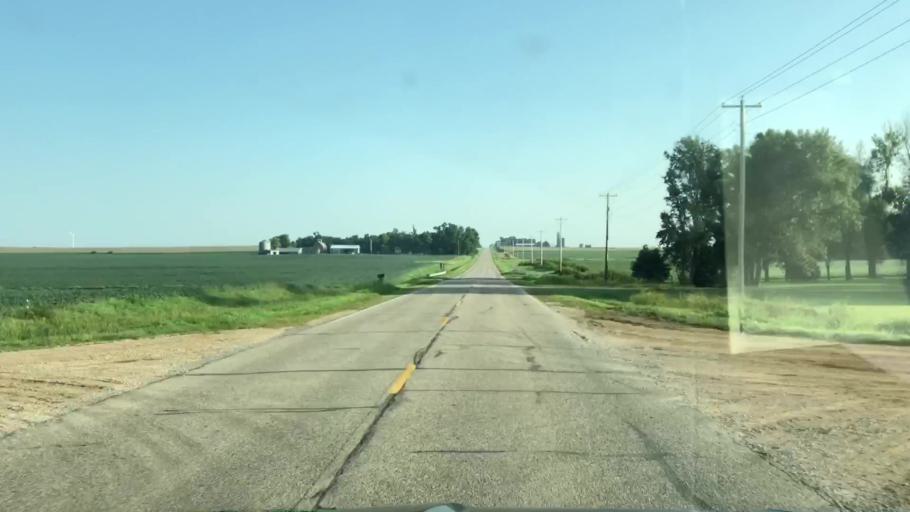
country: US
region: Iowa
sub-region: Lyon County
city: George
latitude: 43.3602
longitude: -95.9983
